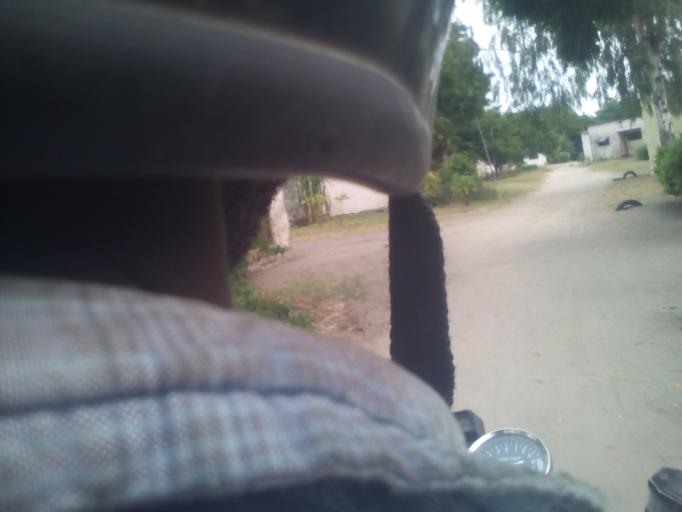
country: TZ
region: Dar es Salaam
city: Dar es Salaam
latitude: -6.8488
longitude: 39.2769
